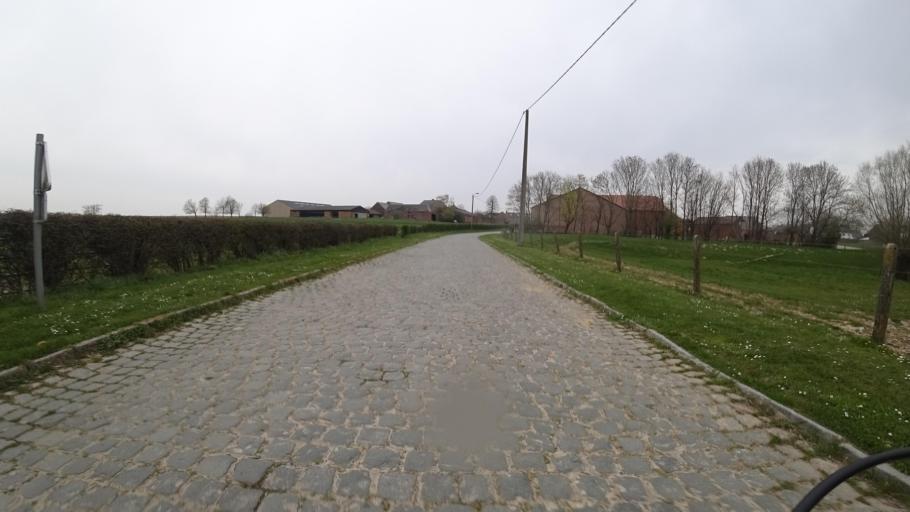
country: BE
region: Wallonia
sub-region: Province du Brabant Wallon
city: Walhain-Saint-Paul
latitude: 50.6124
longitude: 4.6933
